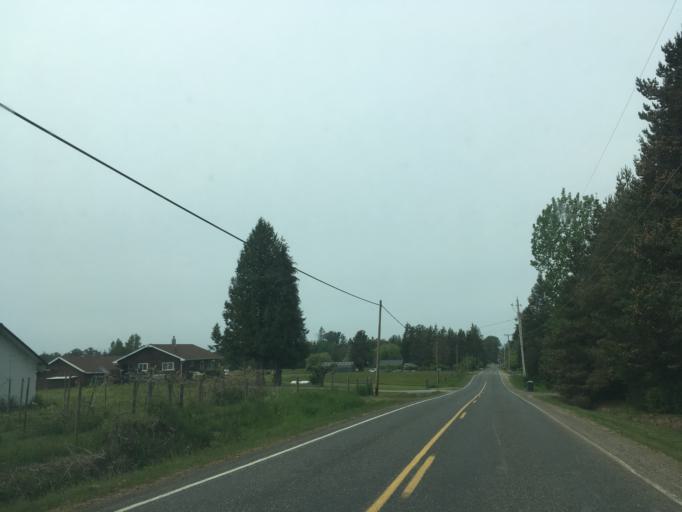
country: US
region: Washington
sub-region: Whatcom County
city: Bellingham
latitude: 48.8188
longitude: -122.4759
